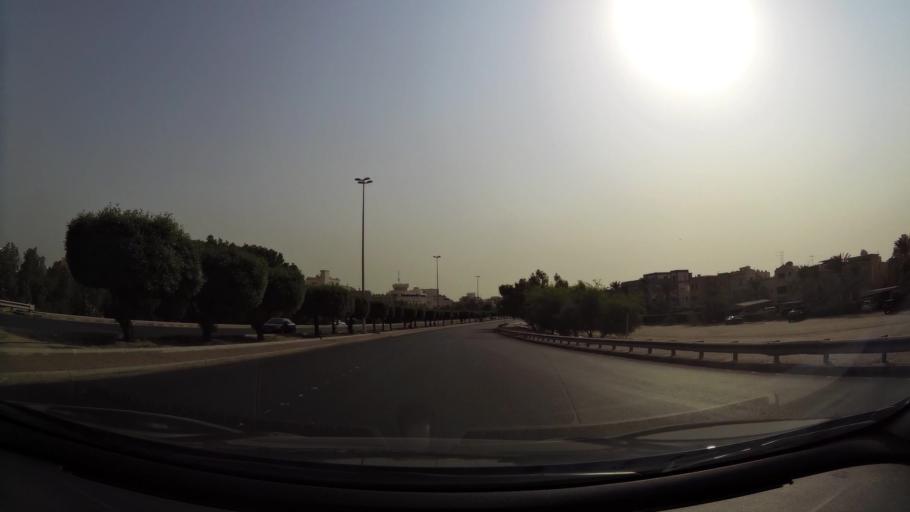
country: KW
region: Mubarak al Kabir
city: Sabah as Salim
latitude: 29.2633
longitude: 48.0668
